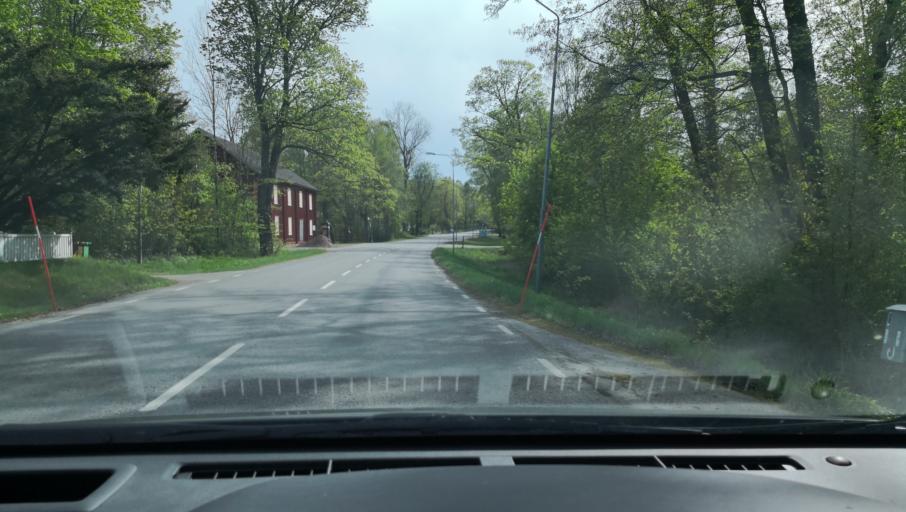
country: SE
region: OErebro
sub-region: Kumla Kommun
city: Kumla
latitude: 59.0970
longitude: 15.1620
